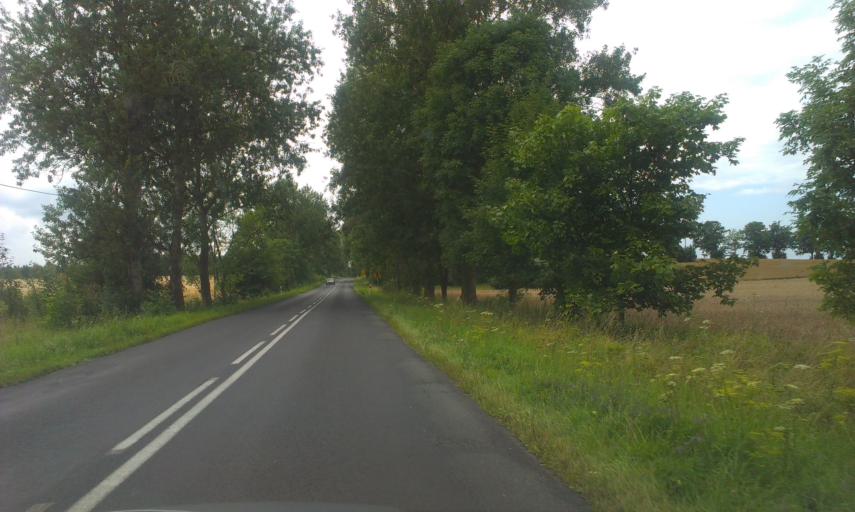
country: PL
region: West Pomeranian Voivodeship
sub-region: Powiat kolobrzeski
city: Dygowo
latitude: 54.1170
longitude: 15.7902
